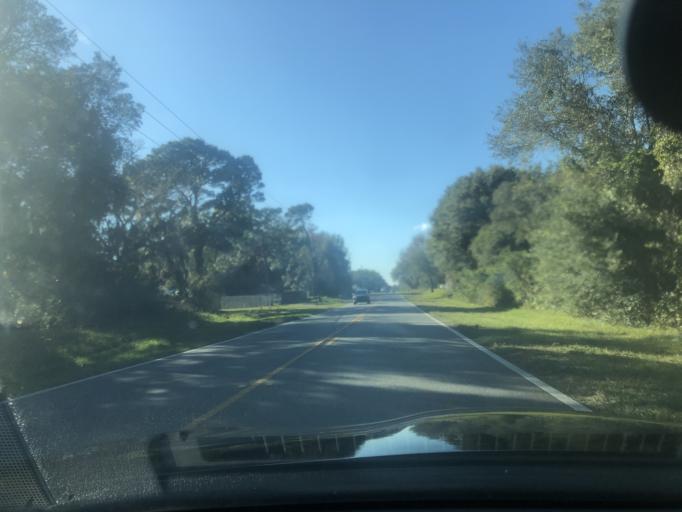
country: US
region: Florida
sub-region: Citrus County
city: Homosassa Springs
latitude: 28.8185
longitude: -82.5387
